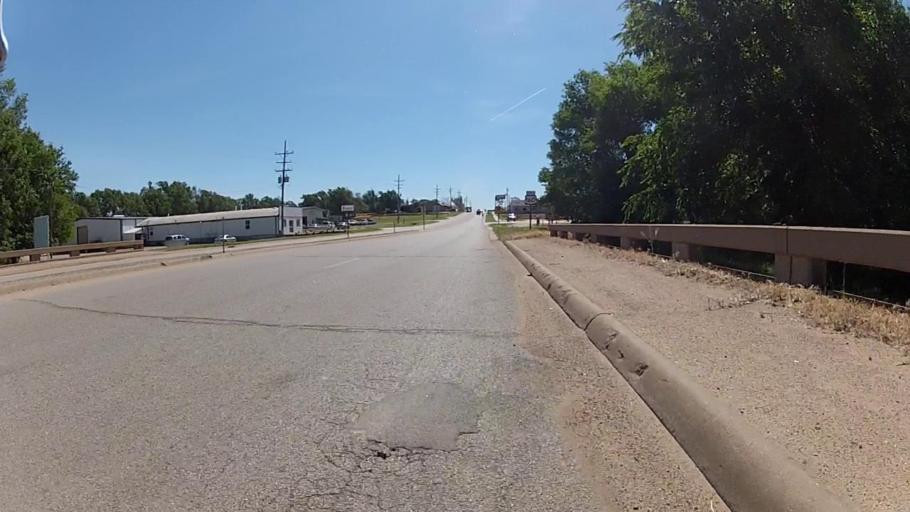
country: US
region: Kansas
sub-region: Barber County
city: Medicine Lodge
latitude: 37.2756
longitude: -98.5861
